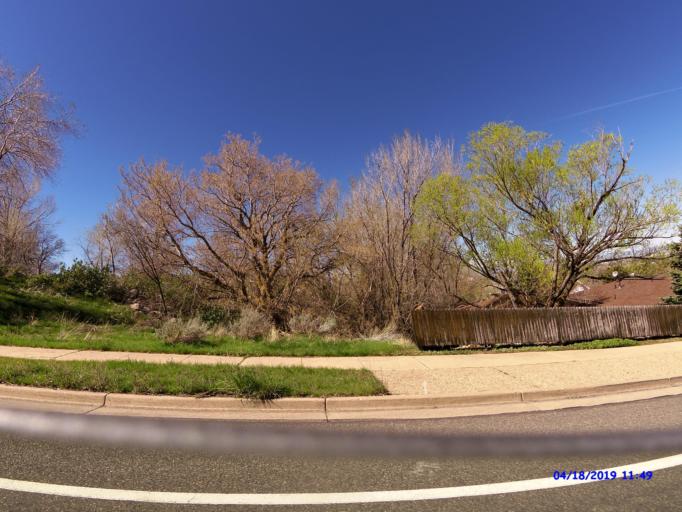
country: US
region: Utah
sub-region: Weber County
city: North Ogden
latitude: 41.2713
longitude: -111.9492
